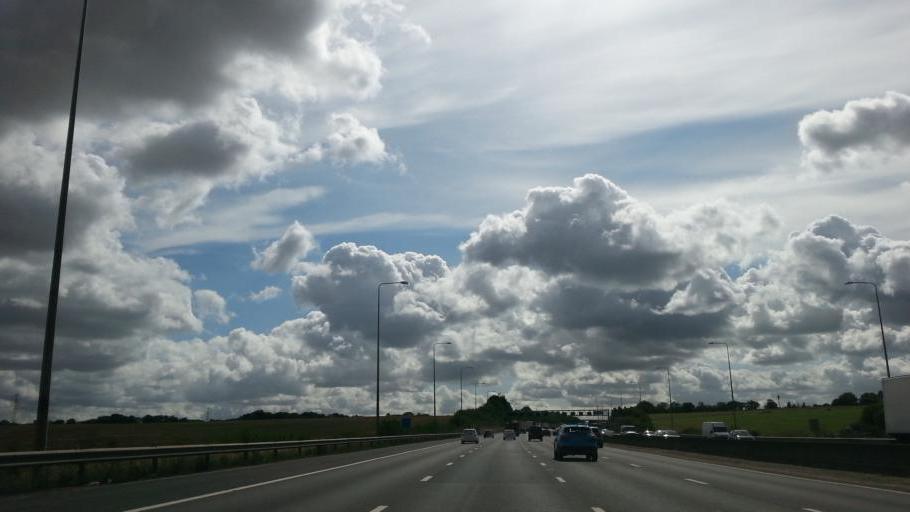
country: GB
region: England
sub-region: Greater London
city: Collier Row
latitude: 51.6514
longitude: 0.1959
